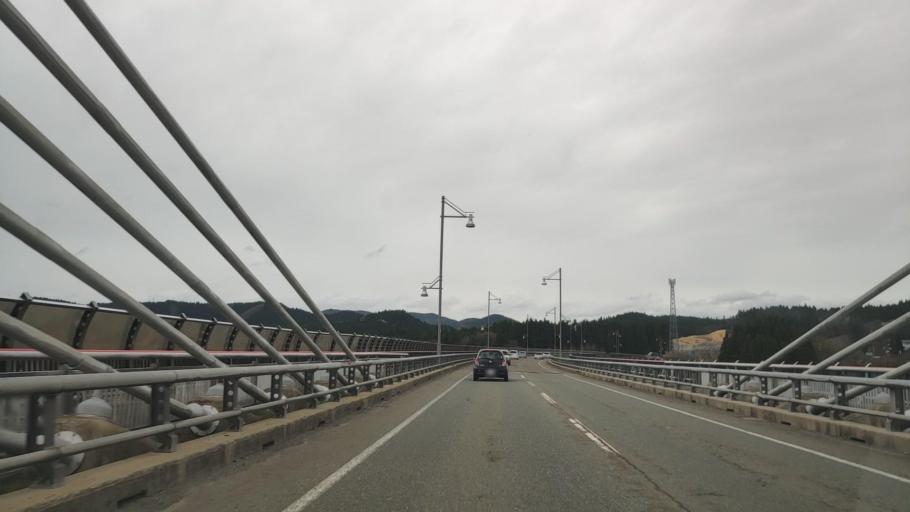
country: JP
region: Akita
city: Takanosu
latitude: 40.2083
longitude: 140.3029
